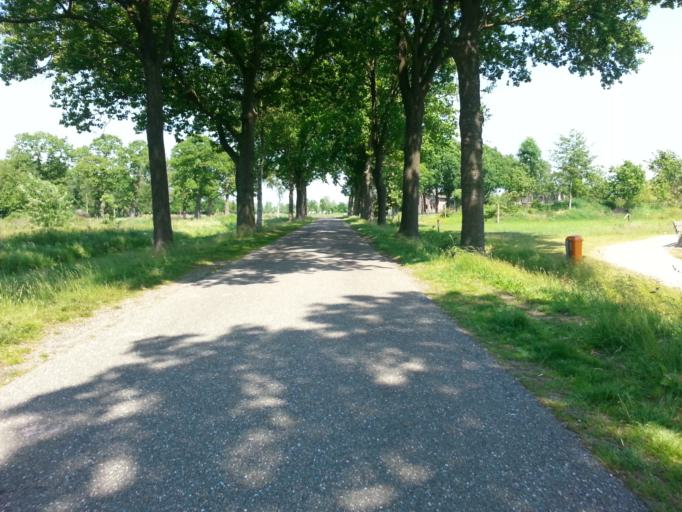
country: NL
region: Gelderland
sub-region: Gemeente Barneveld
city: Terschuur
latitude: 52.1117
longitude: 5.5118
